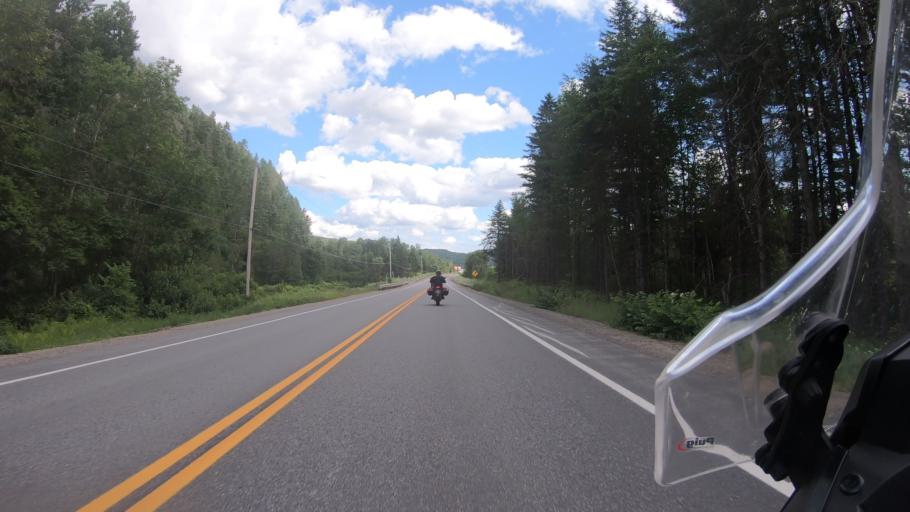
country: CA
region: Quebec
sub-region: Mauricie
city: Saint-Tite
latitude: 46.9899
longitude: -72.9131
